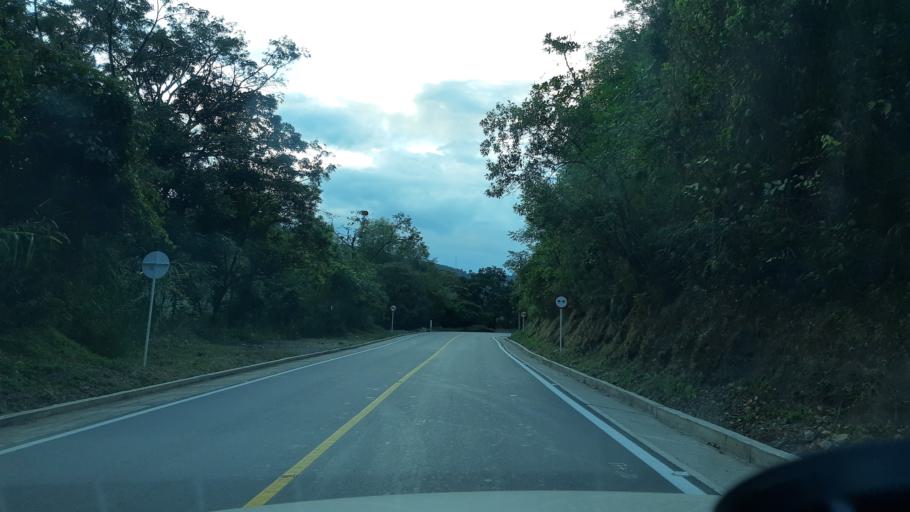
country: CO
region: Boyaca
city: Somondoco
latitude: 4.9859
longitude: -73.3464
